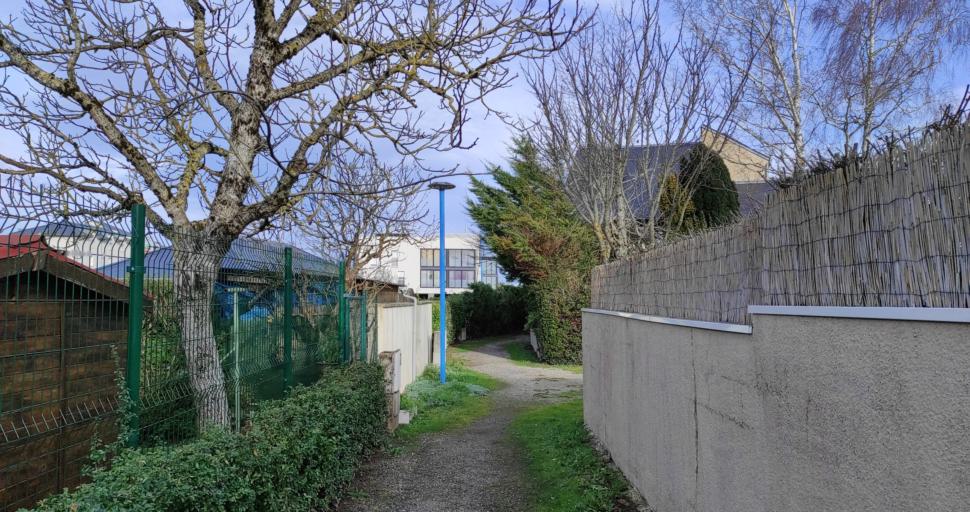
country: FR
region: Midi-Pyrenees
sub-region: Departement de l'Aveyron
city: Rodez
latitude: 44.3789
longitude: 2.5723
